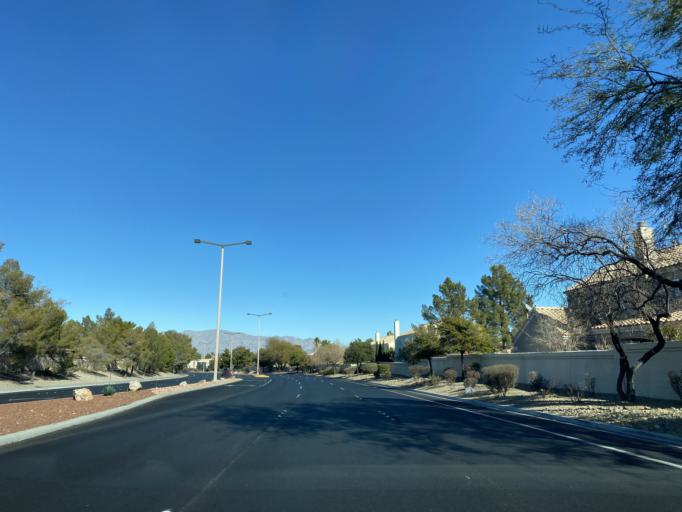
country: US
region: Nevada
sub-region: Clark County
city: Summerlin South
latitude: 36.2020
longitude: -115.2802
